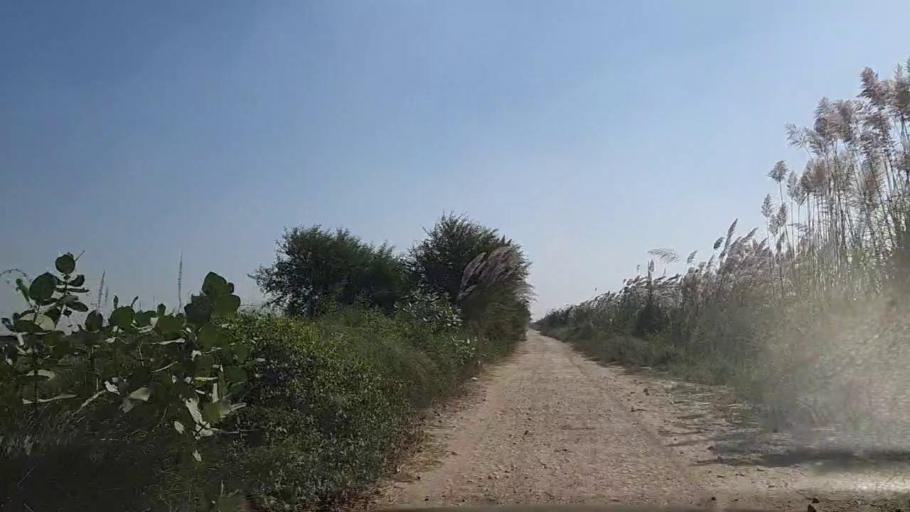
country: PK
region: Sindh
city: Daro Mehar
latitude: 24.8283
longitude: 68.0880
